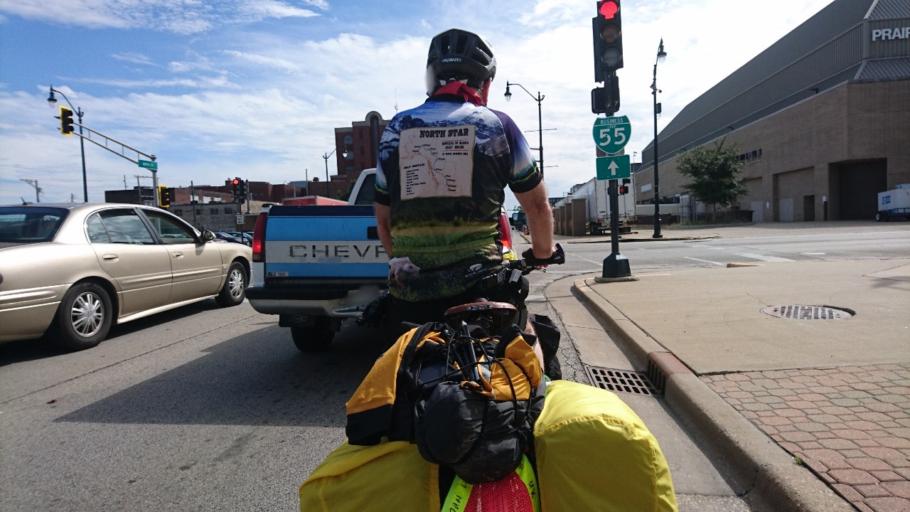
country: US
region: Illinois
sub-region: Sangamon County
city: Springfield
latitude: 39.8020
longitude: -89.6437
